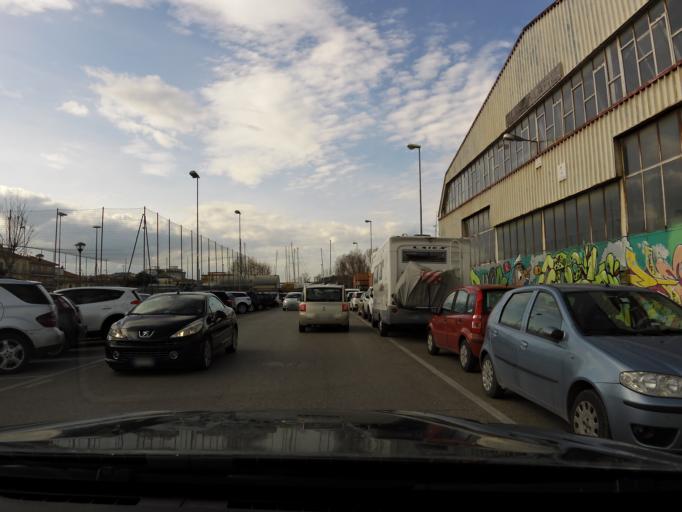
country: IT
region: The Marches
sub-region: Provincia di Macerata
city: Portocivitanova
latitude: 43.3110
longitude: 13.7291
